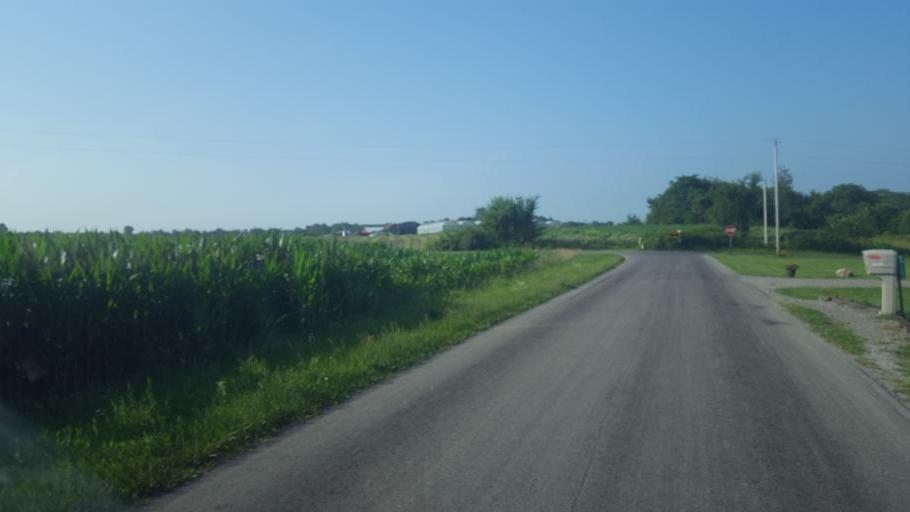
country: US
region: Ohio
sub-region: Hardin County
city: Kenton
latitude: 40.5602
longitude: -83.5846
